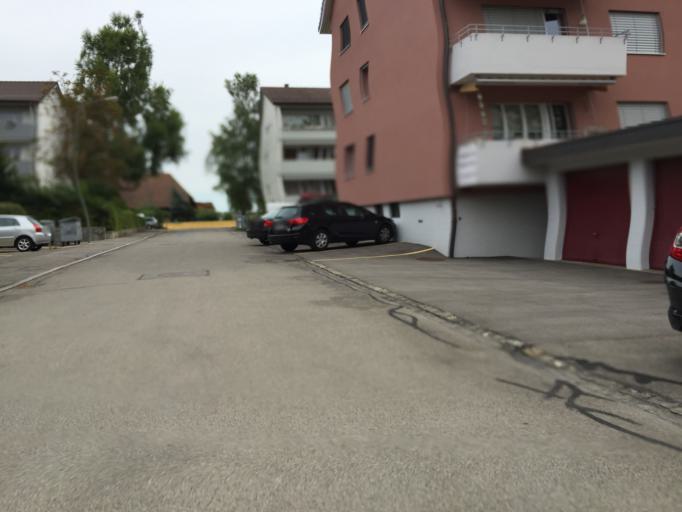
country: CH
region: Bern
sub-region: Bern-Mittelland District
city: Koniz
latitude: 46.9219
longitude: 7.4215
